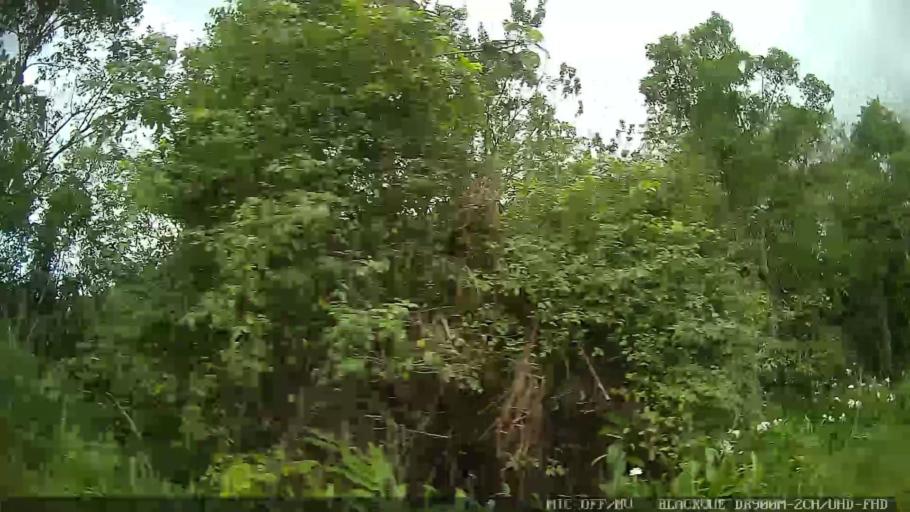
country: BR
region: Sao Paulo
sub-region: Itanhaem
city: Itanhaem
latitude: -24.1418
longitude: -46.7766
